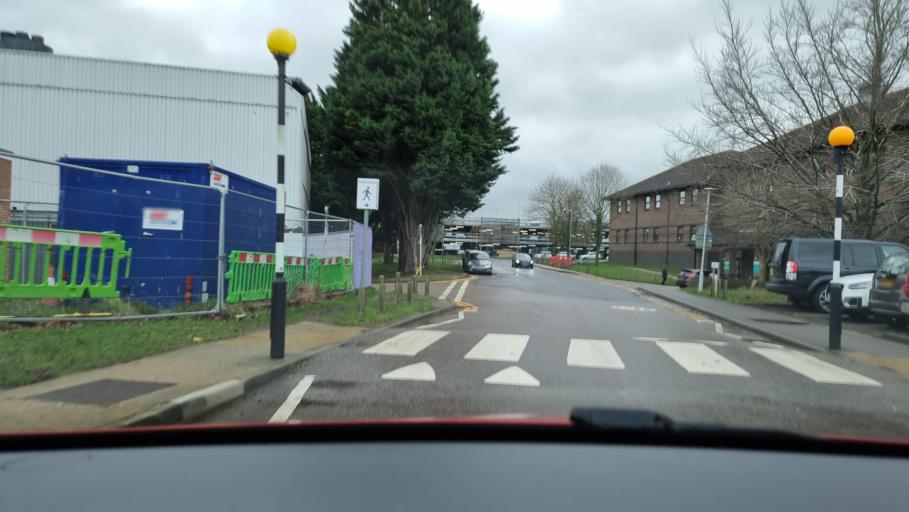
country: GB
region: England
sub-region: Buckinghamshire
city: Aylesbury
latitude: 51.7985
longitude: -0.7997
